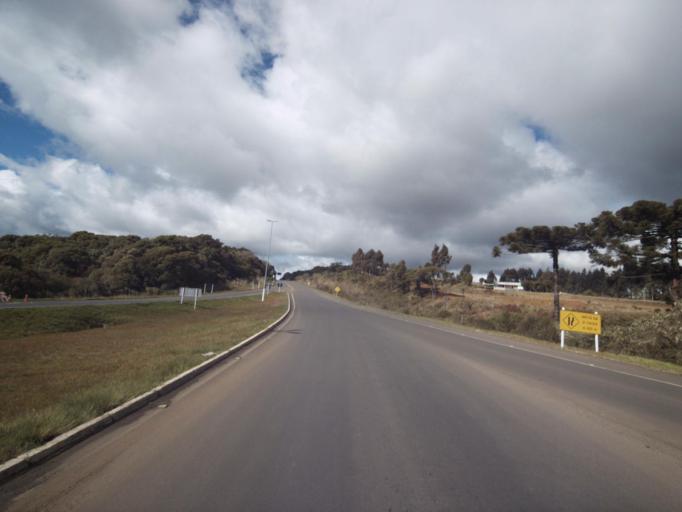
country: BR
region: Santa Catarina
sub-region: Concordia
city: Concordia
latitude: -26.9699
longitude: -51.8541
